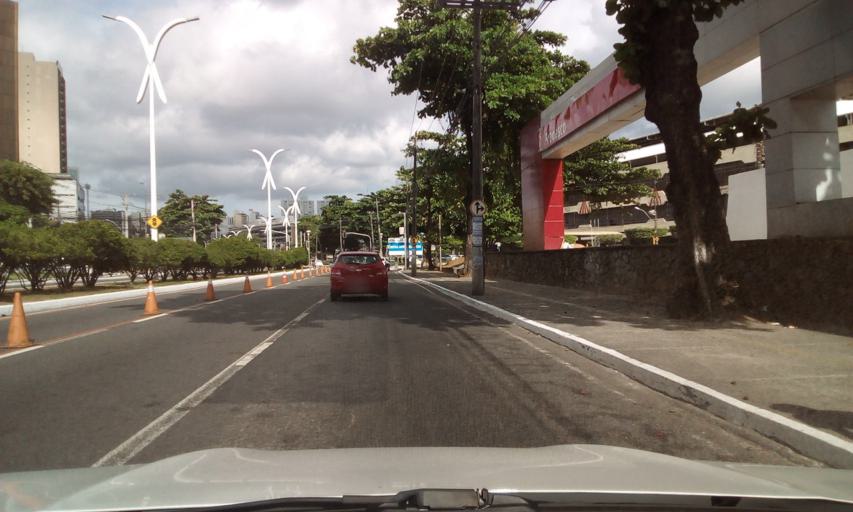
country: BR
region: Bahia
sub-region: Salvador
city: Salvador
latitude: -12.9978
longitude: -38.4630
